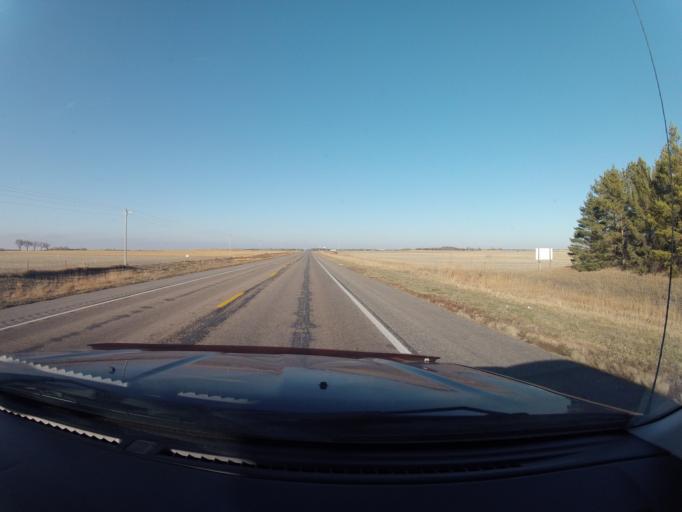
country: US
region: Nebraska
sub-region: Kearney County
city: Minden
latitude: 40.5790
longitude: -98.9518
